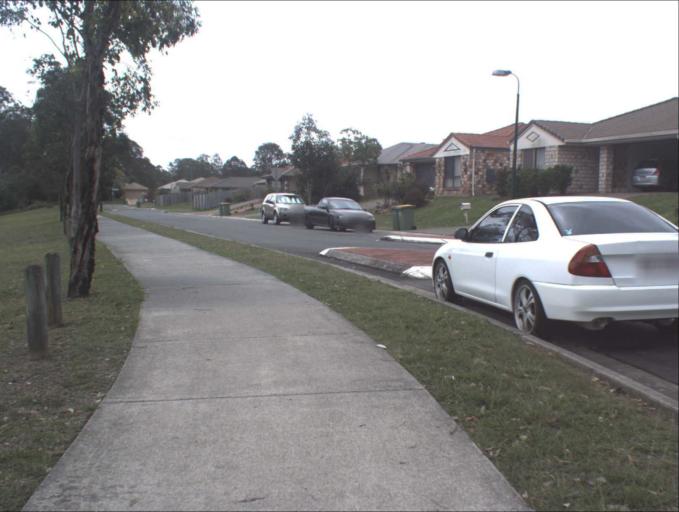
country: AU
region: Queensland
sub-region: Logan
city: Waterford West
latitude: -27.6962
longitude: 153.1131
